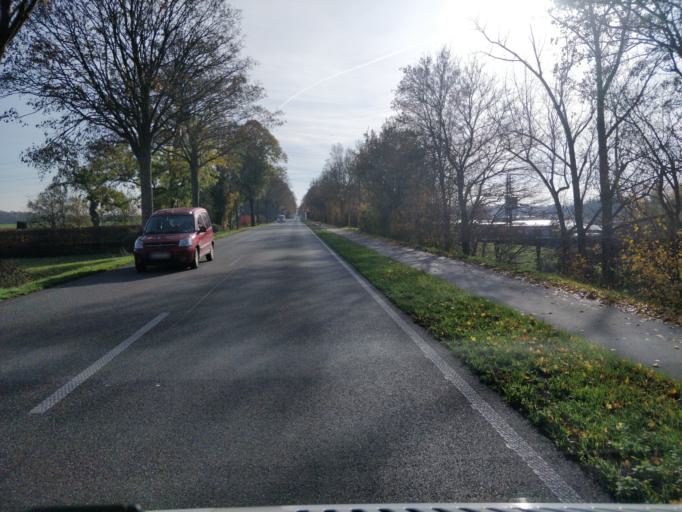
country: DE
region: North Rhine-Westphalia
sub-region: Regierungsbezirk Dusseldorf
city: Mehrhoog
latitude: 51.7490
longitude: 6.4893
